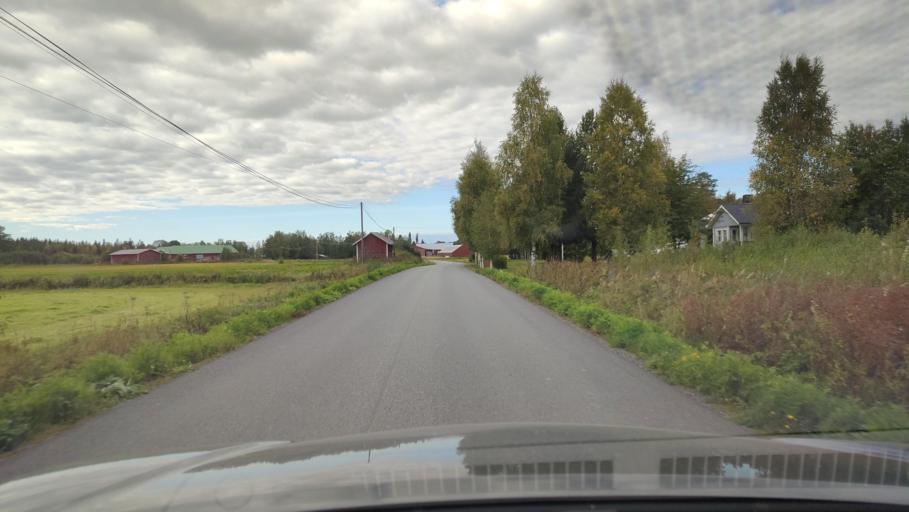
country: FI
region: Southern Ostrobothnia
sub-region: Suupohja
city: Karijoki
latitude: 62.2375
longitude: 21.5865
